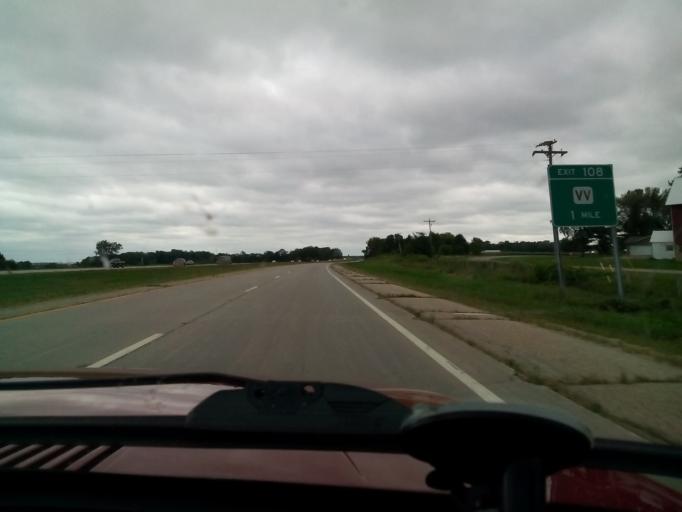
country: US
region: Wisconsin
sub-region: Dane County
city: Marshall
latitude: 43.2546
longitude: -89.1263
